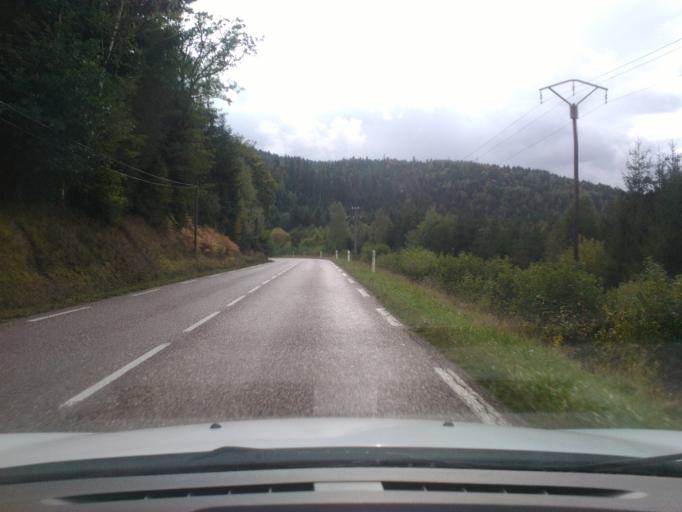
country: FR
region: Lorraine
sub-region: Departement des Vosges
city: Taintrux
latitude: 48.2640
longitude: 6.8130
